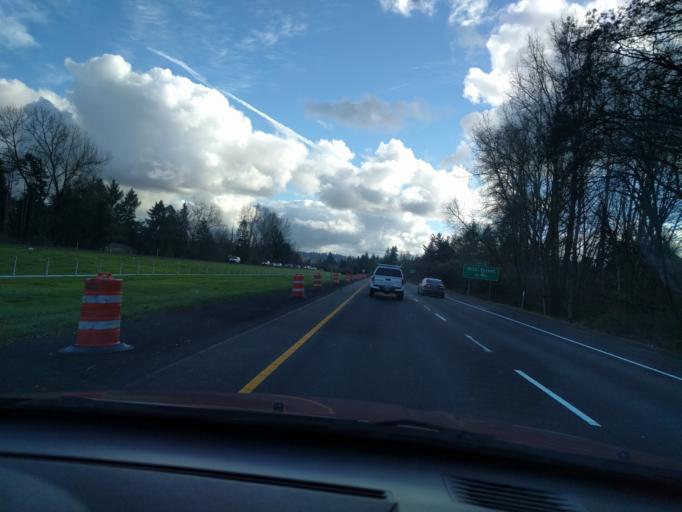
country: US
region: Oregon
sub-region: Clackamas County
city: West Linn
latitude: 45.3553
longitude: -122.6643
